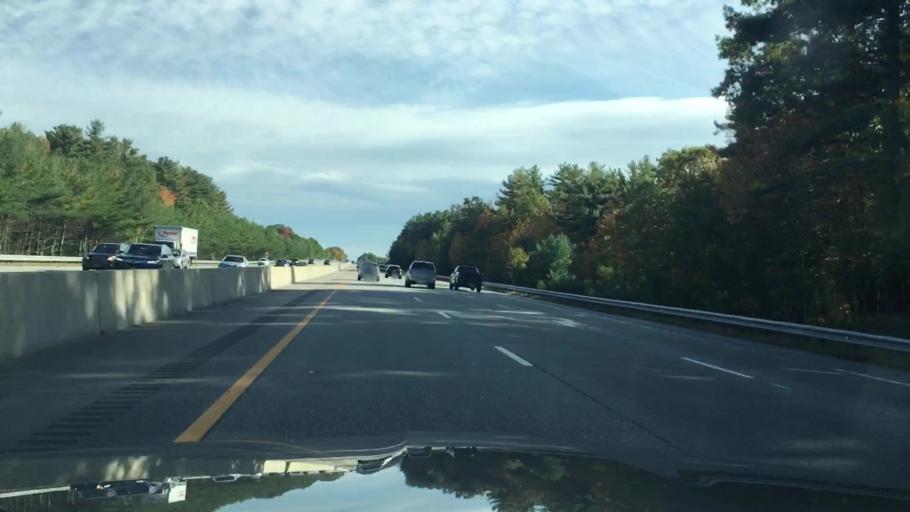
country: US
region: New Hampshire
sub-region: Merrimack County
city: Bow Bog
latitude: 43.1334
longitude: -71.4903
